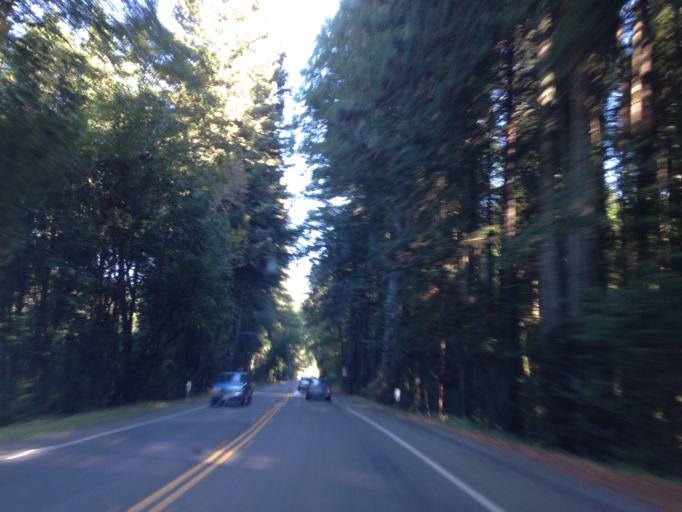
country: US
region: California
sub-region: Sonoma County
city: Monte Rio
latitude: 38.4812
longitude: -123.0014
